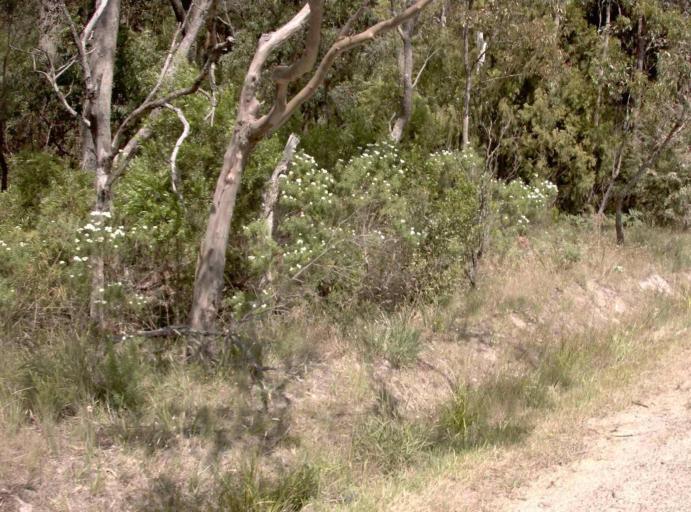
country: AU
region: Victoria
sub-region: Latrobe
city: Traralgon
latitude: -38.2987
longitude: 146.5381
